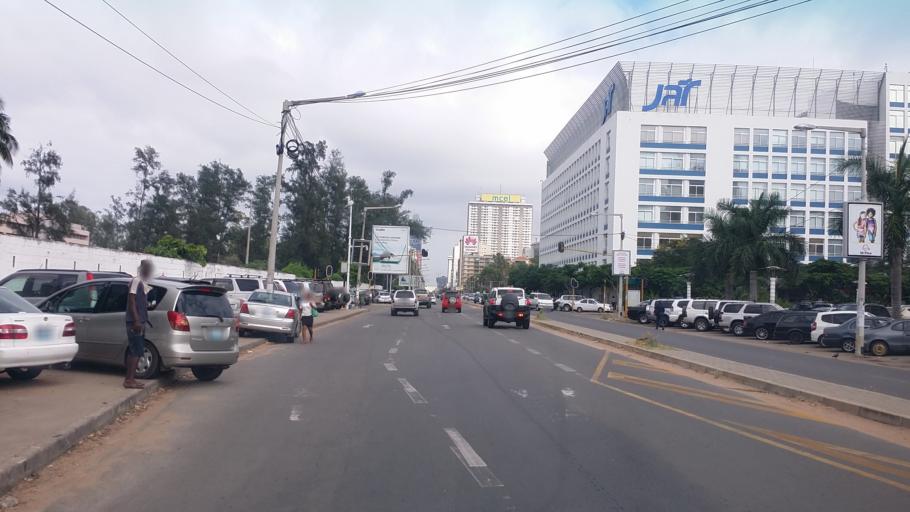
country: MZ
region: Maputo City
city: Maputo
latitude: -25.9791
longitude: 32.5819
